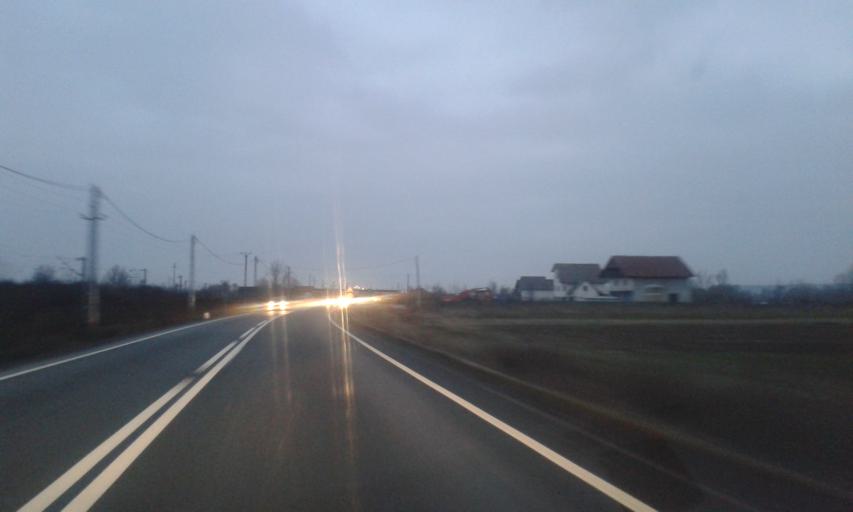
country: RO
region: Gorj
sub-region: Comuna Turcinesti
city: Turcinesti
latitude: 45.1059
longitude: 23.3394
